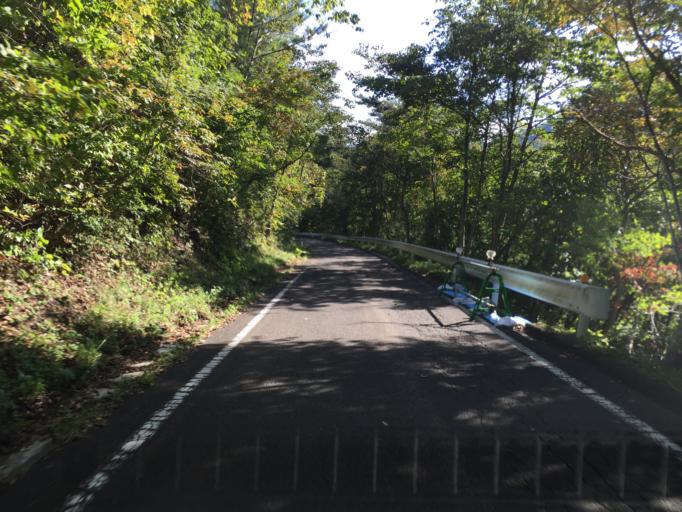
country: JP
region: Fukushima
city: Yanagawamachi-saiwaicho
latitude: 37.8353
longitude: 140.7001
